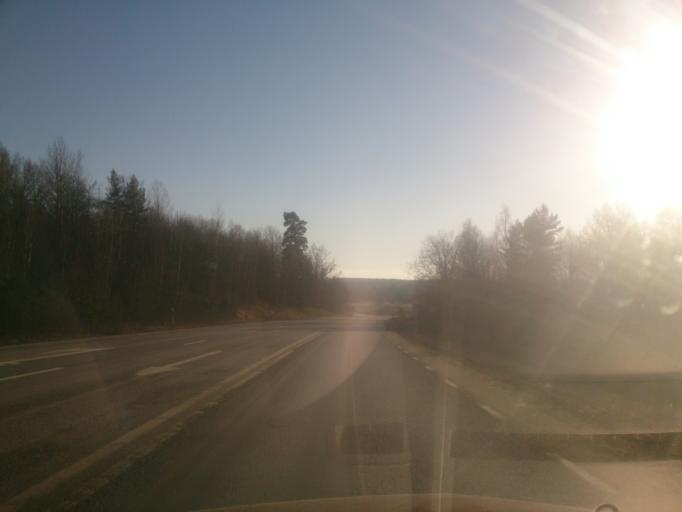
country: SE
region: OEstergoetland
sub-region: Norrkopings Kommun
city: Kimstad
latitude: 58.5169
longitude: 15.9843
